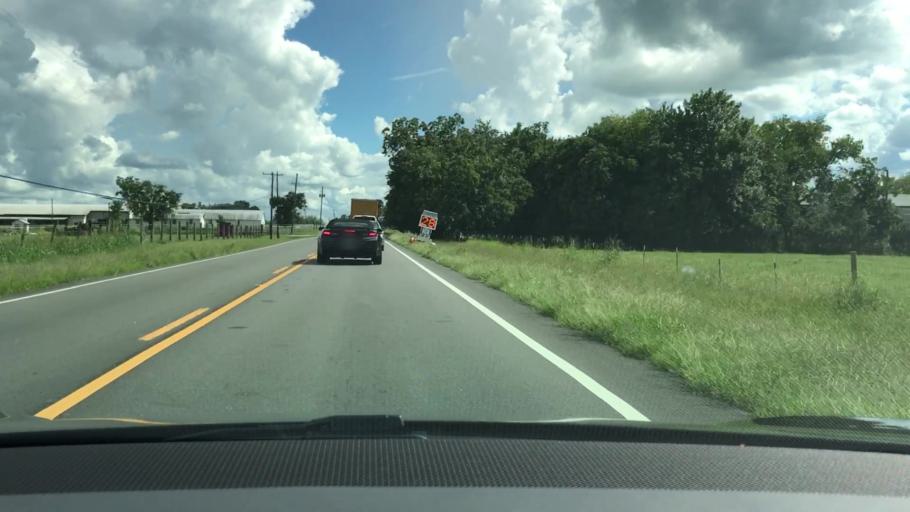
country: US
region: Alabama
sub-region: Montgomery County
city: Pike Road
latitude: 32.2873
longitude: -86.1026
